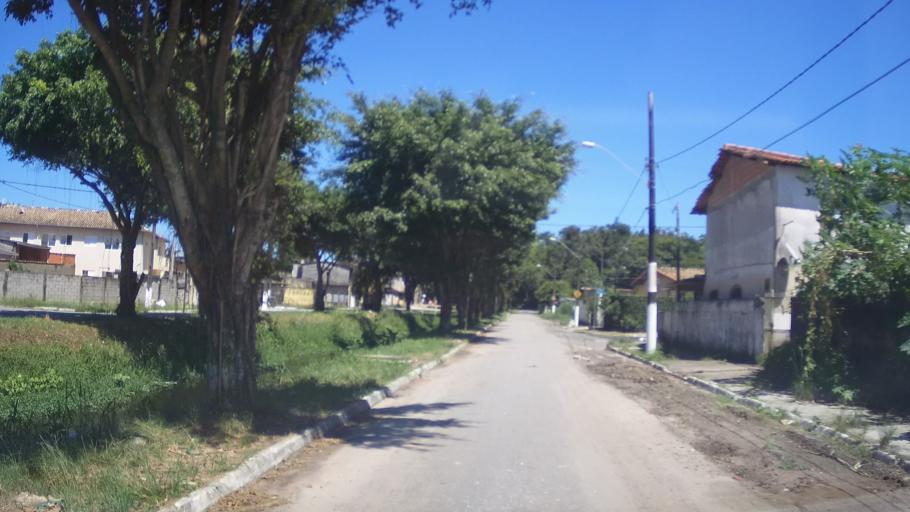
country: BR
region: Sao Paulo
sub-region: Mongagua
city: Mongagua
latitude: -24.0768
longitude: -46.5948
